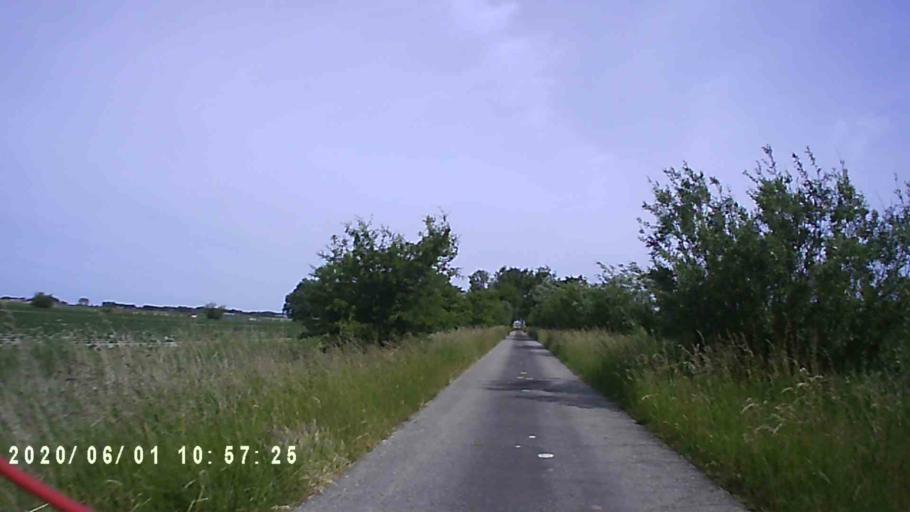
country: NL
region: Friesland
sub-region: Gemeente Franekeradeel
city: Sexbierum
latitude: 53.1990
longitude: 5.4927
